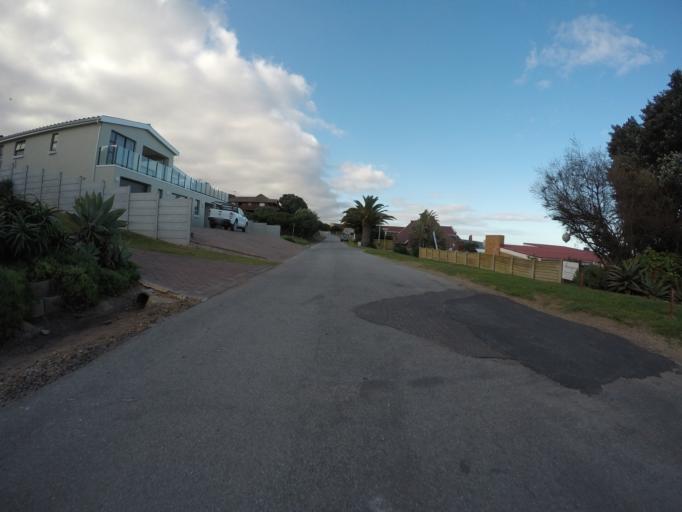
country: ZA
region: Western Cape
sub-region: Eden District Municipality
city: Riversdale
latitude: -34.4242
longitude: 21.3432
